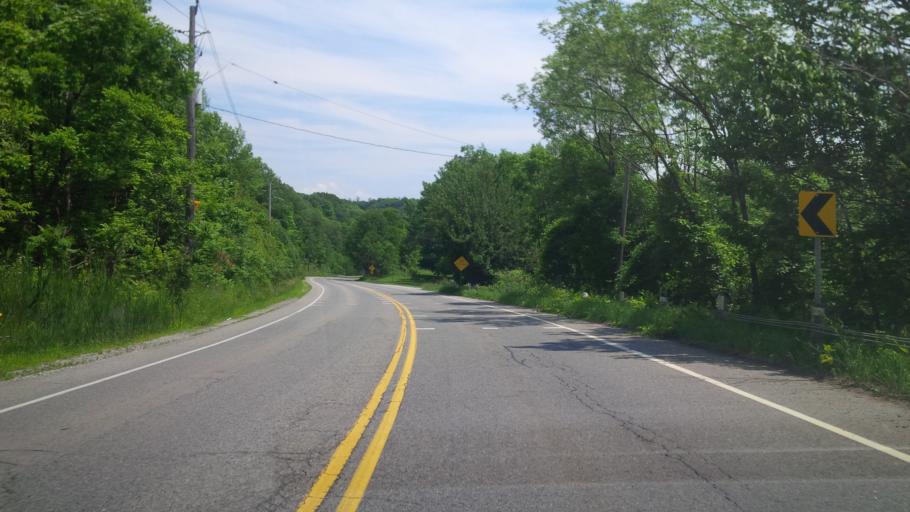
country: CA
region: Ontario
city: Burlington
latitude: 43.4262
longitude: -79.8348
